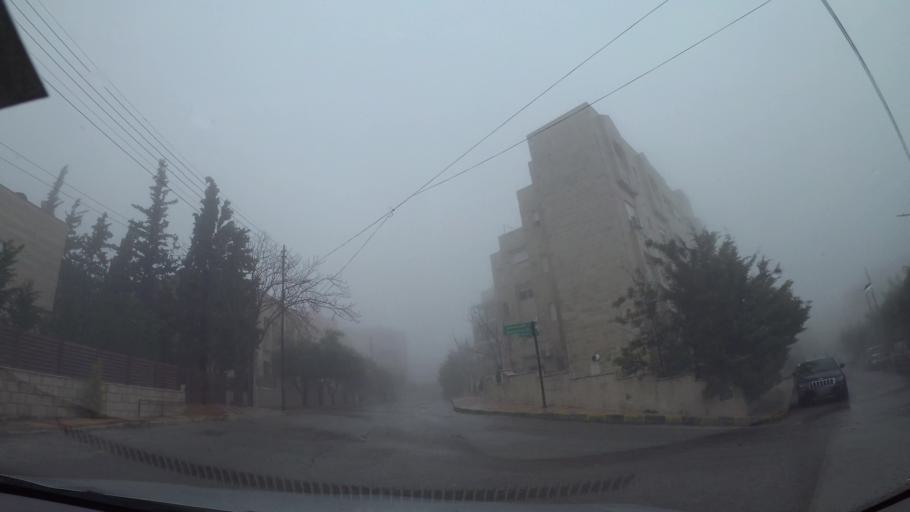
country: JO
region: Amman
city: Al Jubayhah
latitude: 32.0092
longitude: 35.8813
